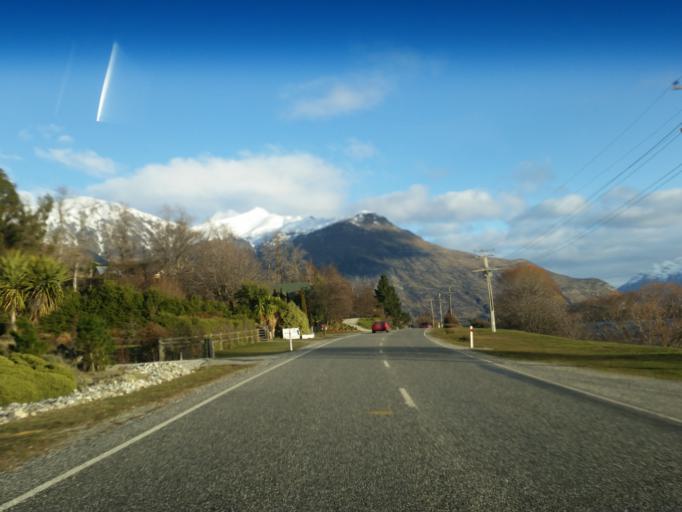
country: NZ
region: Otago
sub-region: Queenstown-Lakes District
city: Arrowtown
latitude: -44.9706
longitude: 168.8175
